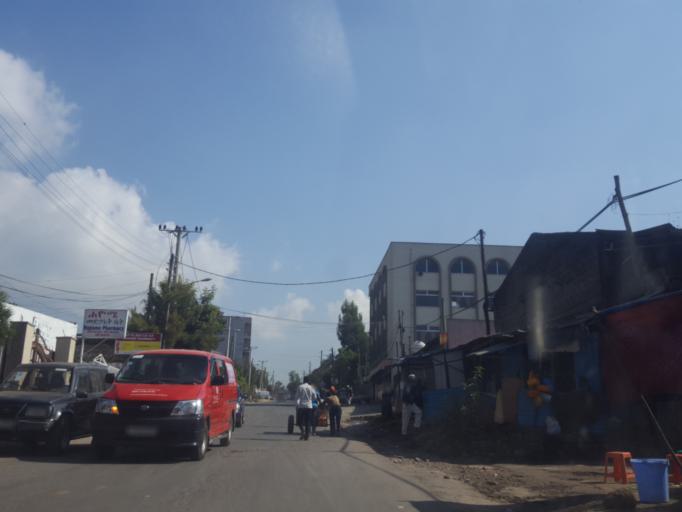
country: ET
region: Adis Abeba
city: Addis Ababa
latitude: 9.0492
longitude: 38.7260
